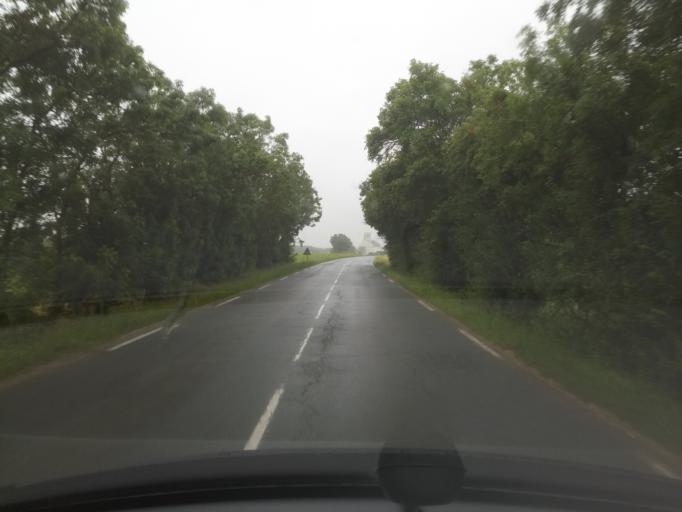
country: FR
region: Poitou-Charentes
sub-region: Departement de la Charente-Maritime
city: Saint-Jean-de-Liversay
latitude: 46.2330
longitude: -0.8809
